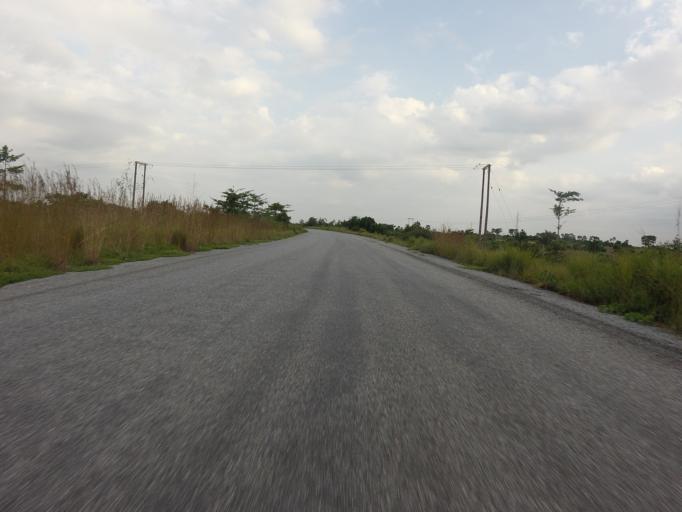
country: GH
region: Volta
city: Ho
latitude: 6.3858
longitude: 0.5286
